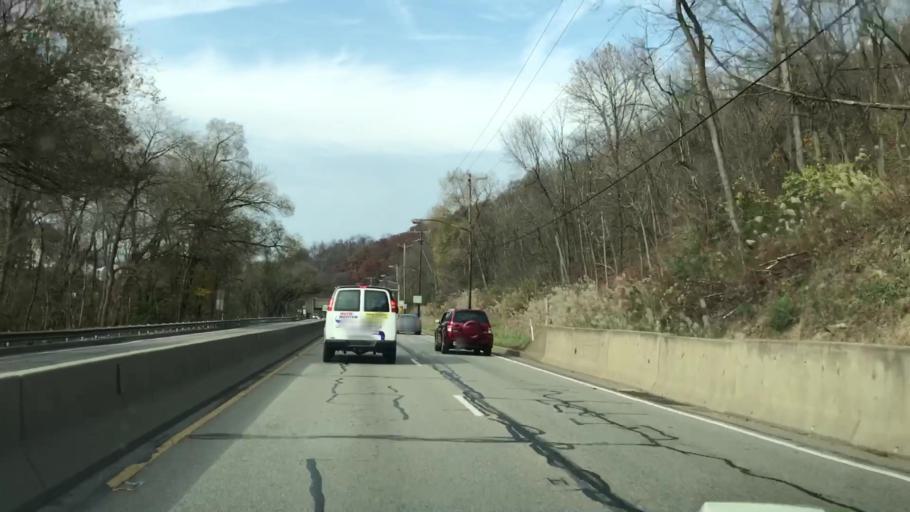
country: US
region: Pennsylvania
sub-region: Allegheny County
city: Pittsburgh
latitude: 40.4226
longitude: -80.0166
